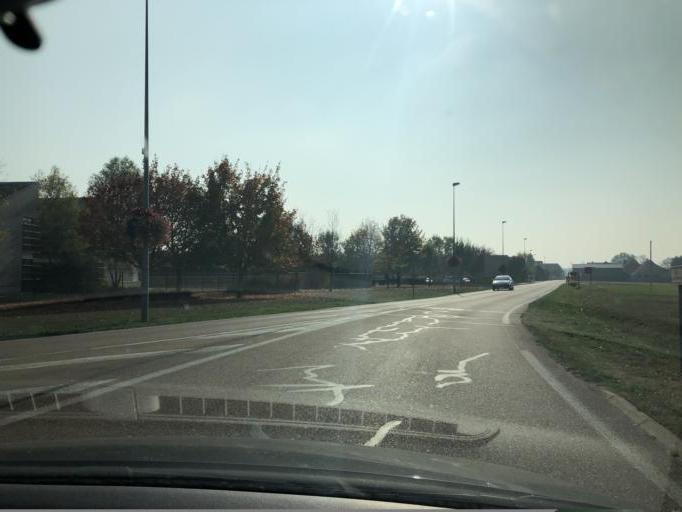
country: FR
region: Bourgogne
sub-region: Departement de l'Yonne
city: Saint-Clement
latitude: 48.2217
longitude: 3.2876
